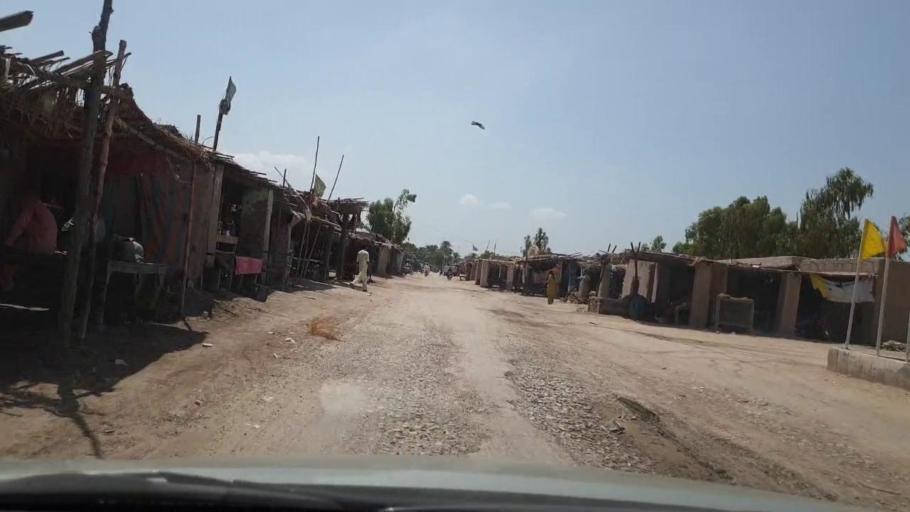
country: PK
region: Sindh
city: Pano Aqil
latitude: 27.6695
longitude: 69.0883
